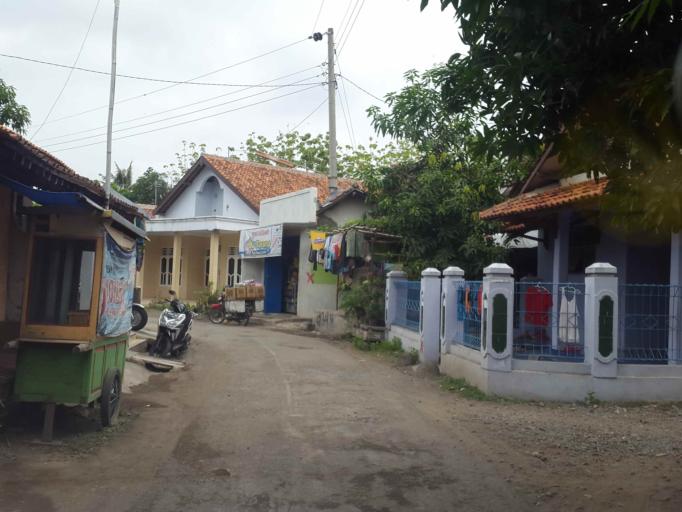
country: ID
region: Central Java
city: Adiwerna
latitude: -6.9355
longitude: 109.1209
